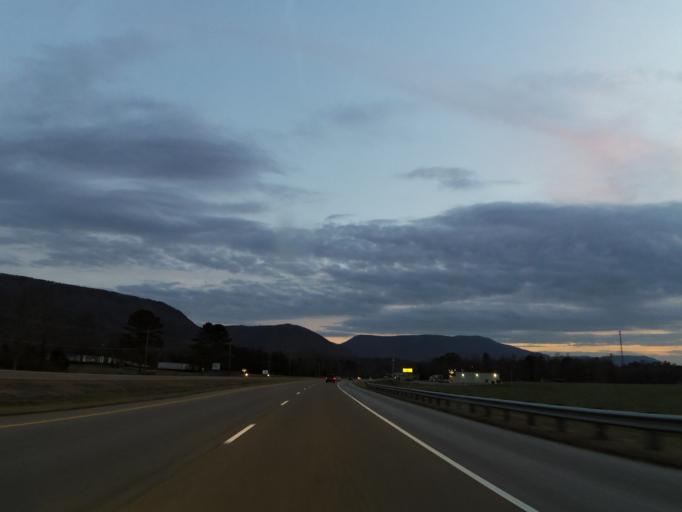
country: US
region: Tennessee
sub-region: McMinn County
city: Etowah
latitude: 35.2765
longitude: -84.5464
